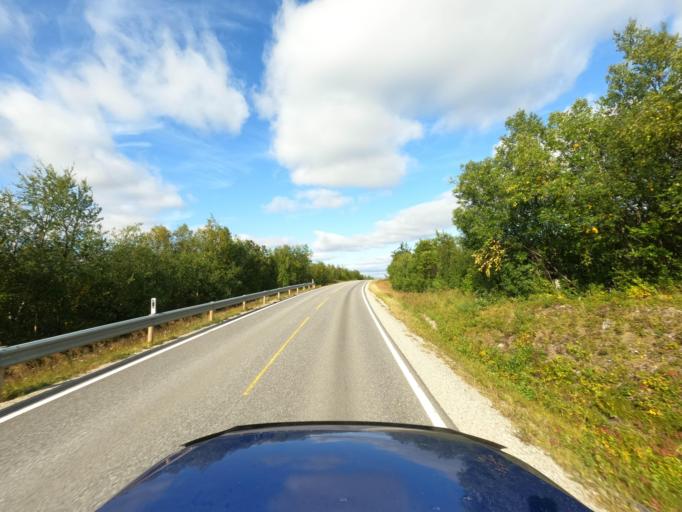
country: NO
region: Finnmark Fylke
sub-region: Porsanger
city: Lakselv
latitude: 69.9454
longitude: 24.9593
